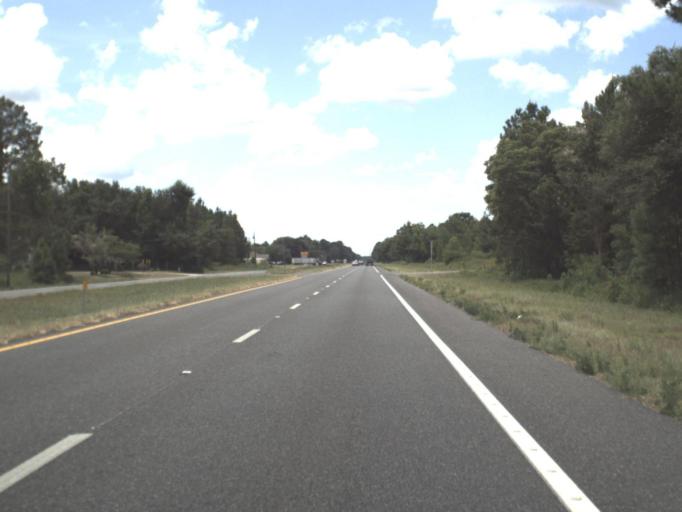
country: US
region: Florida
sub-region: Taylor County
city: Perry
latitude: 30.1572
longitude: -83.6198
